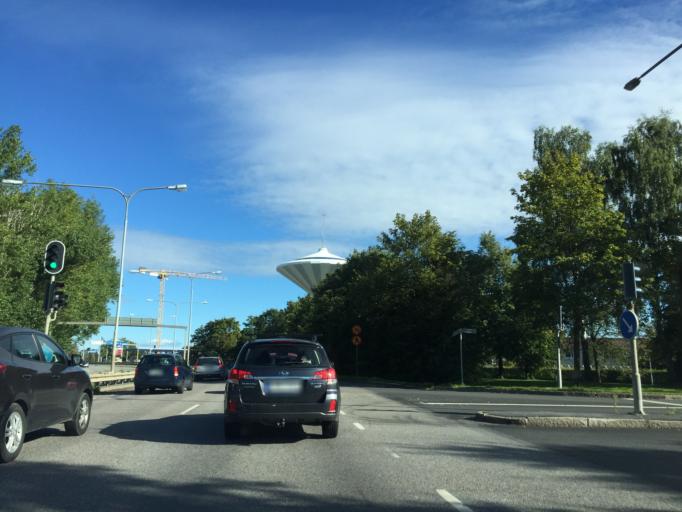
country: SE
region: OErebro
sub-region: Orebro Kommun
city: Orebro
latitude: 59.2867
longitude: 15.2212
